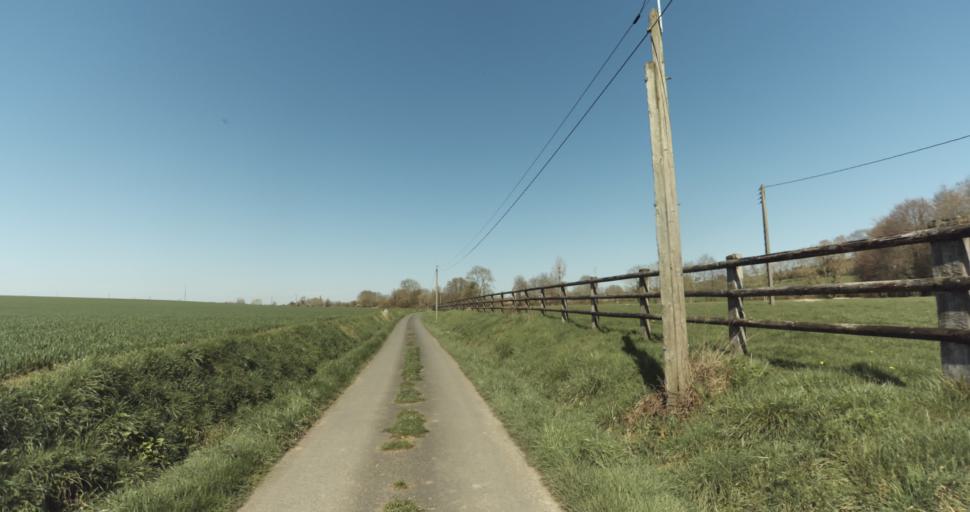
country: FR
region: Lower Normandy
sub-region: Departement du Calvados
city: Saint-Pierre-sur-Dives
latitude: 49.0024
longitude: 0.0254
